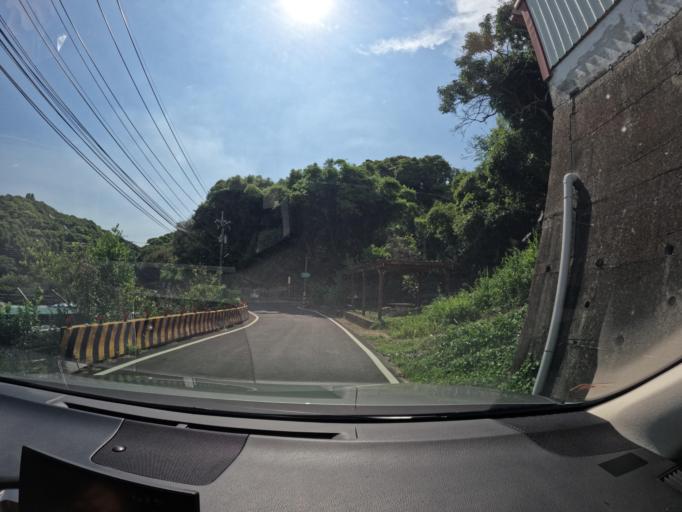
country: TW
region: Taiwan
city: Fengyuan
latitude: 24.3125
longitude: 120.7520
